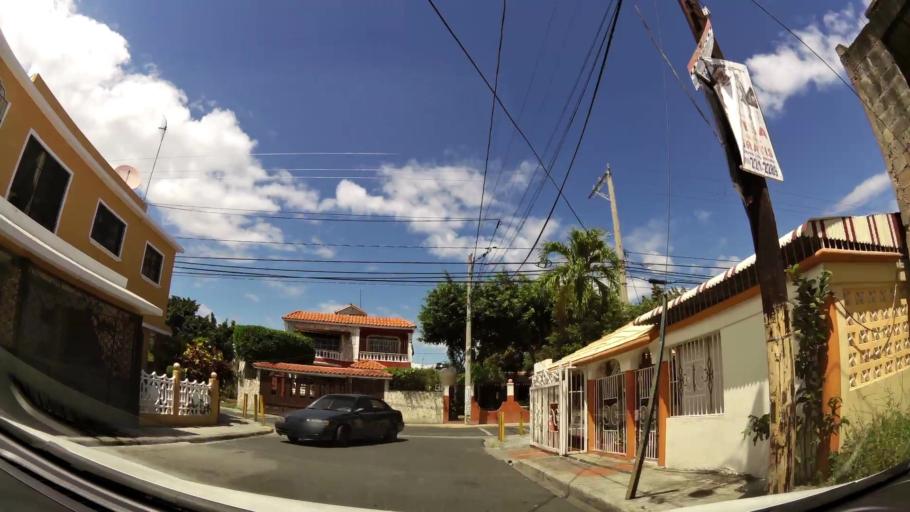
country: DO
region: San Cristobal
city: San Cristobal
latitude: 18.4198
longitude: -70.0966
